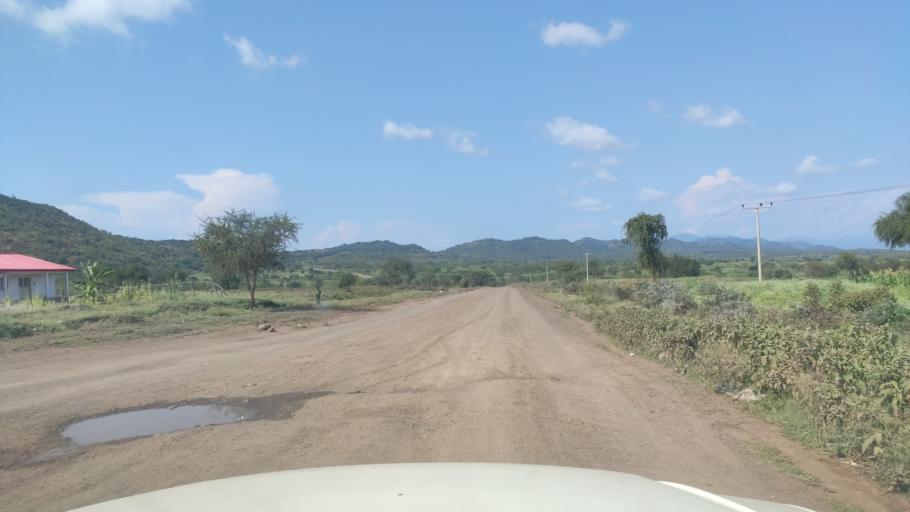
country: ET
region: Southern Nations, Nationalities, and People's Region
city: Felege Neway
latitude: 6.3718
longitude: 37.0863
